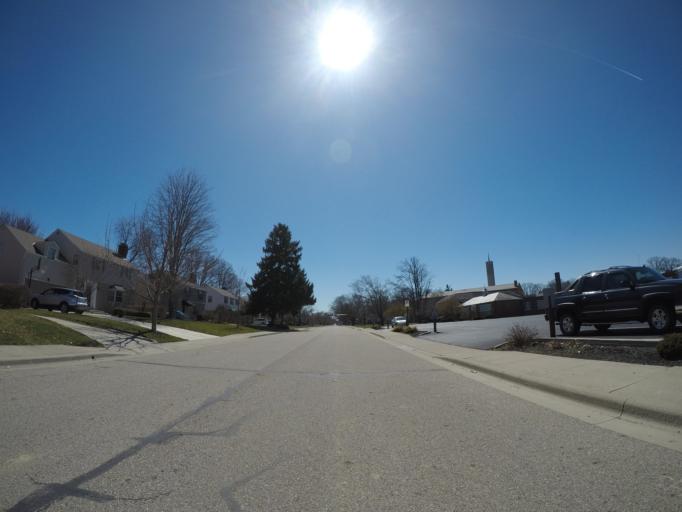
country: US
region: Ohio
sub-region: Franklin County
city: Upper Arlington
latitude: 40.0136
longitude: -83.0600
